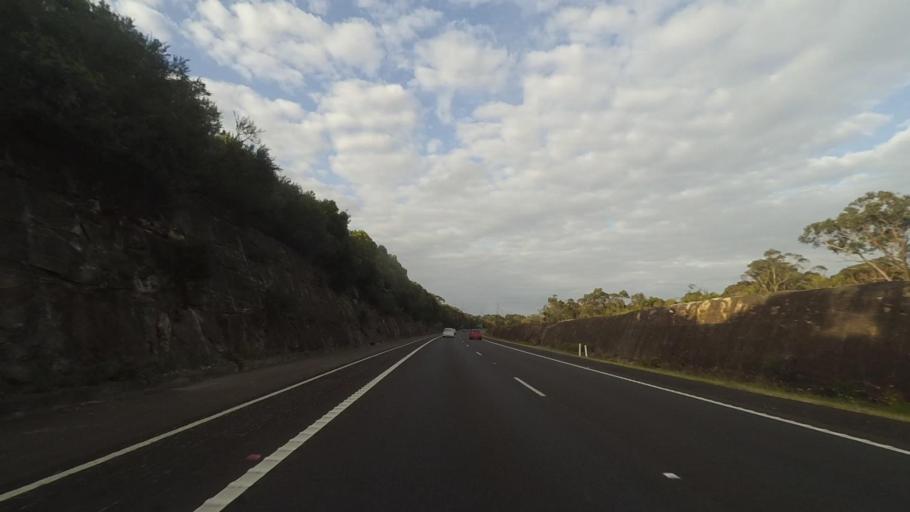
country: AU
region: New South Wales
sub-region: Wollongong
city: Helensburgh
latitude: -34.2296
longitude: 150.9474
